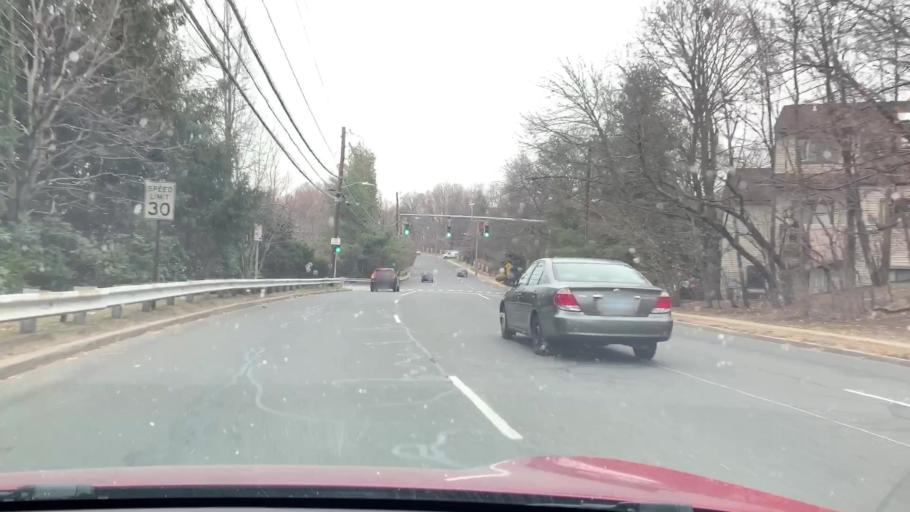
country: US
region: Connecticut
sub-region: Fairfield County
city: Stamford
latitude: 41.0684
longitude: -73.5445
